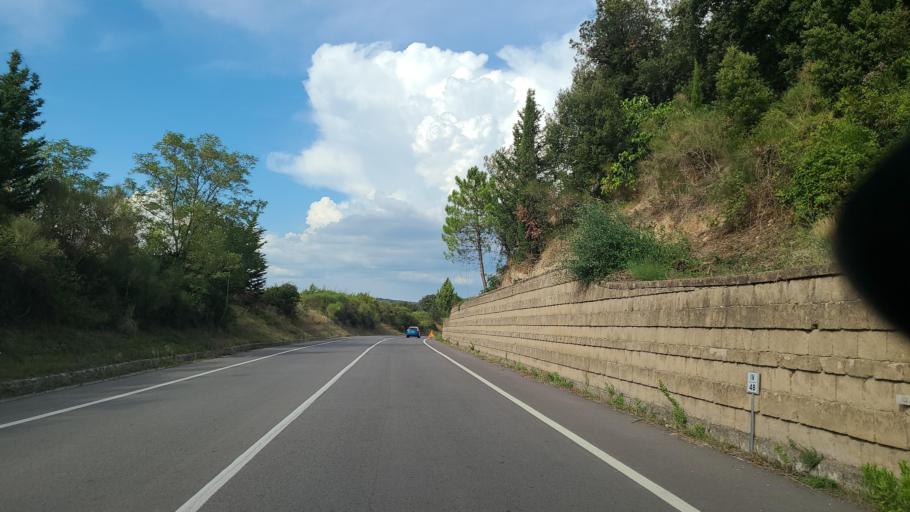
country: IT
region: Tuscany
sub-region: Province of Pisa
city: Volterra
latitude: 43.3930
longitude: 10.9546
